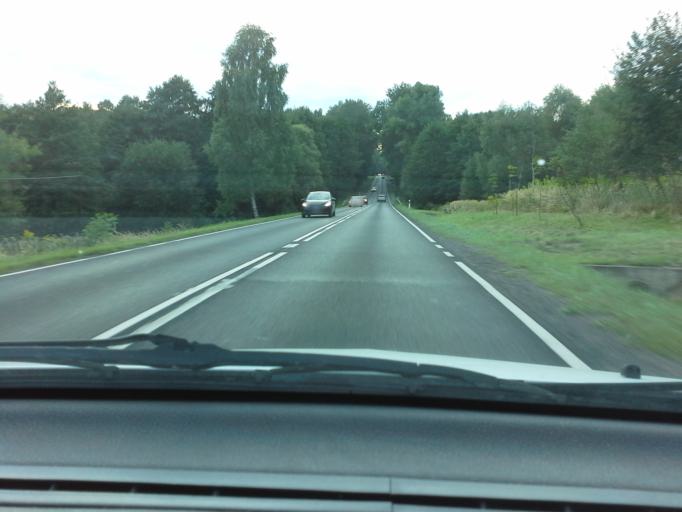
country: PL
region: Lesser Poland Voivodeship
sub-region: Powiat krakowski
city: Filipowice
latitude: 50.1392
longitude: 19.5568
